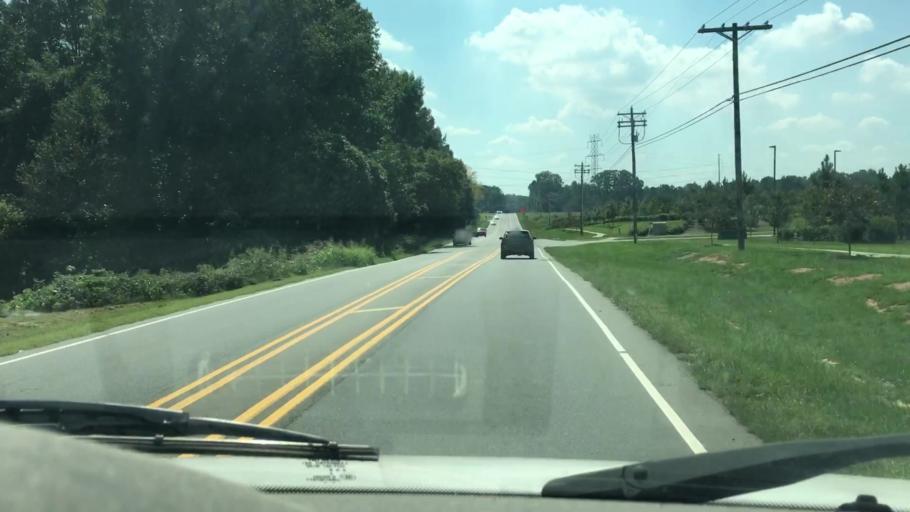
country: US
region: North Carolina
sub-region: Mecklenburg County
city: Huntersville
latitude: 35.3804
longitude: -80.8534
